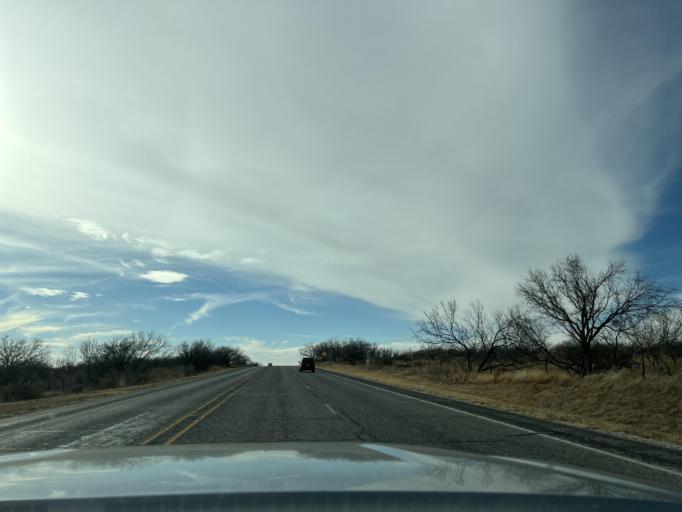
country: US
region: Texas
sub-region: Fisher County
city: Roby
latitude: 32.7567
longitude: -100.3266
